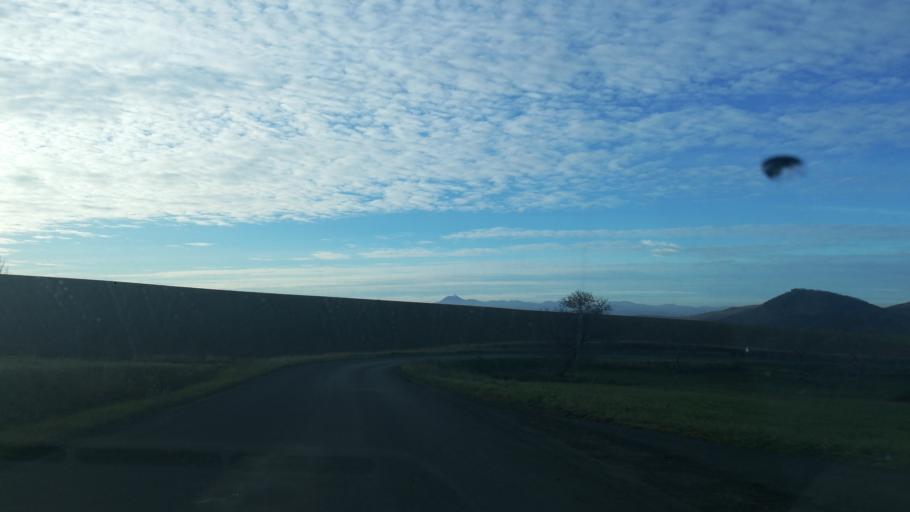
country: FR
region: Auvergne
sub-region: Departement du Puy-de-Dome
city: Billom
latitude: 45.7039
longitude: 3.3529
